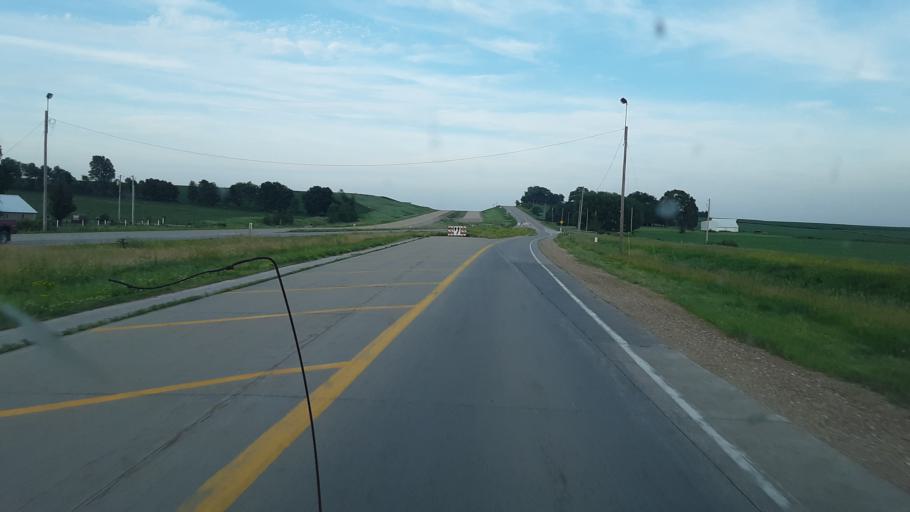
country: US
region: Iowa
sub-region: Tama County
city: Tama
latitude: 41.9642
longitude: -92.5315
